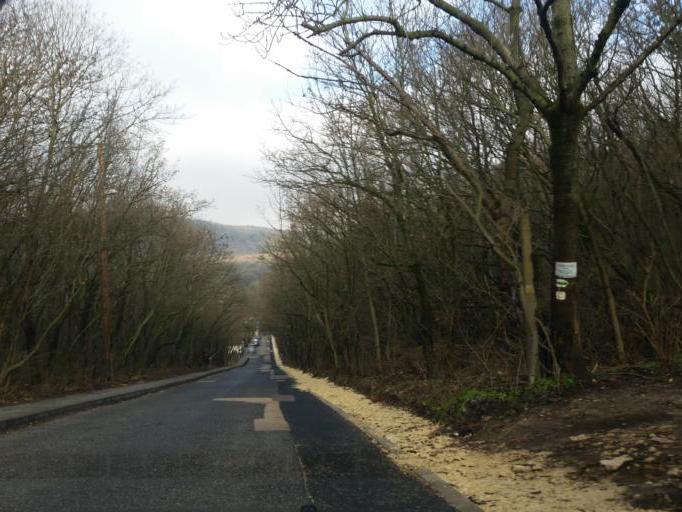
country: HU
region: Budapest
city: Budapest II. keruelet
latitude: 47.5346
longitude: 18.9928
